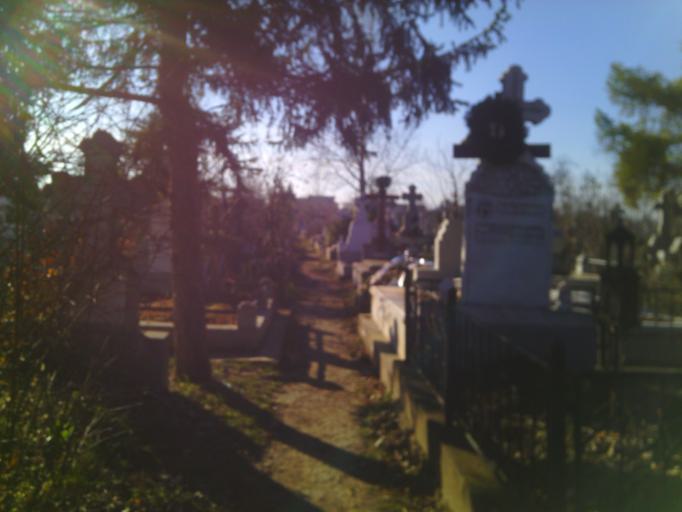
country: RO
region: Ilfov
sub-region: Comuna Popesti-Leordeni
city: Popesti-Leordeni
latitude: 44.3835
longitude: 26.1633
